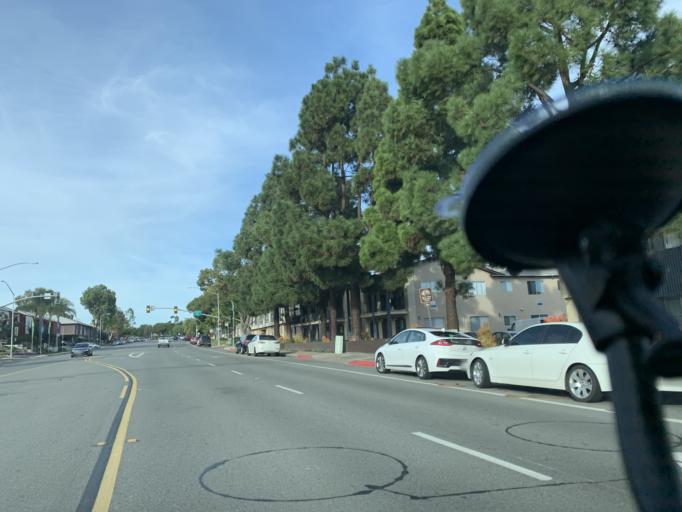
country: US
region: California
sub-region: San Diego County
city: San Diego
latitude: 32.8042
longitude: -117.1287
